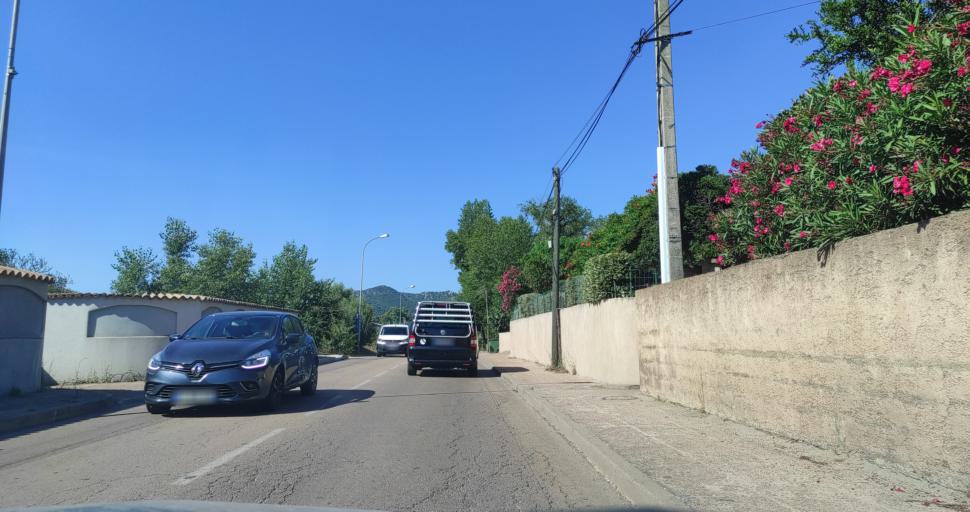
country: FR
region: Corsica
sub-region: Departement de la Corse-du-Sud
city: Porto-Vecchio
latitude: 41.5829
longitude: 9.2789
